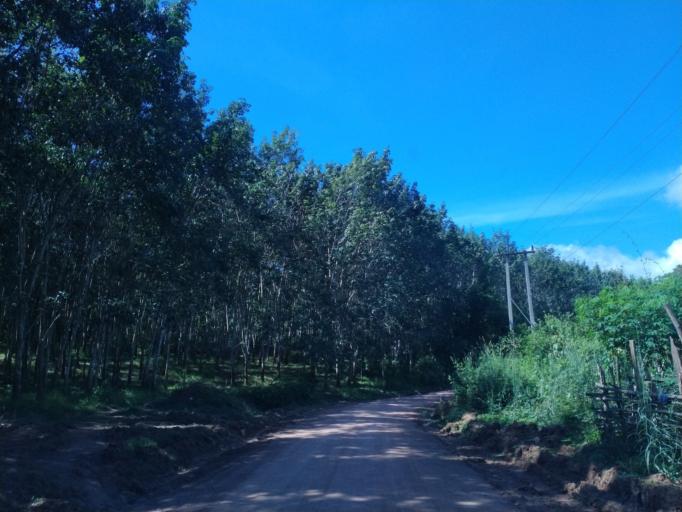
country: TH
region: Changwat Bueng Kan
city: Pak Khat
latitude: 18.6383
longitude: 102.9962
